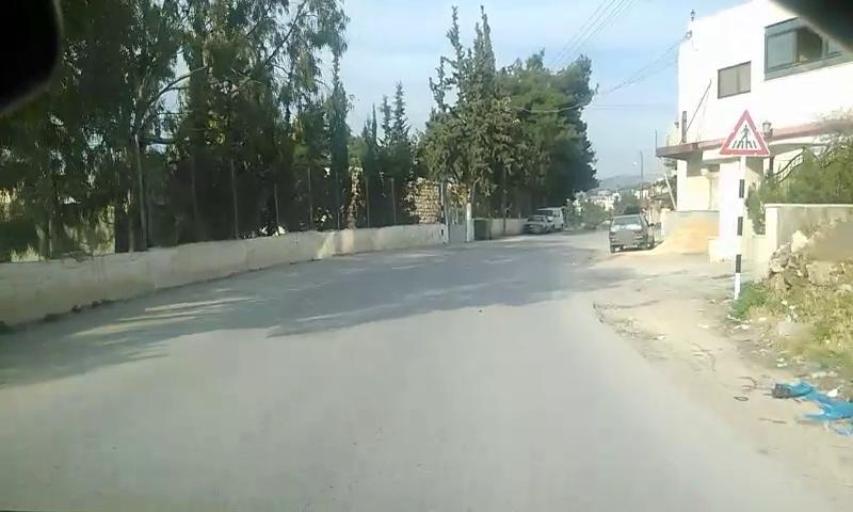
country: PS
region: West Bank
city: Nuba
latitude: 31.6091
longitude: 35.0387
